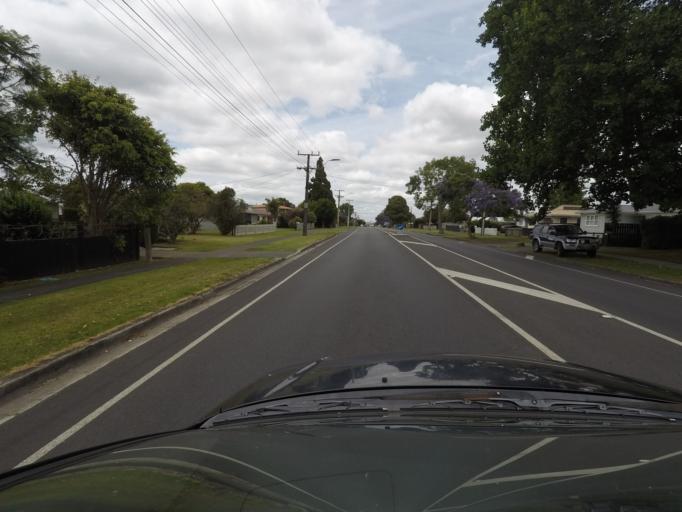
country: NZ
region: Northland
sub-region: Whangarei
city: Whangarei
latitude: -35.6877
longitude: 174.3270
